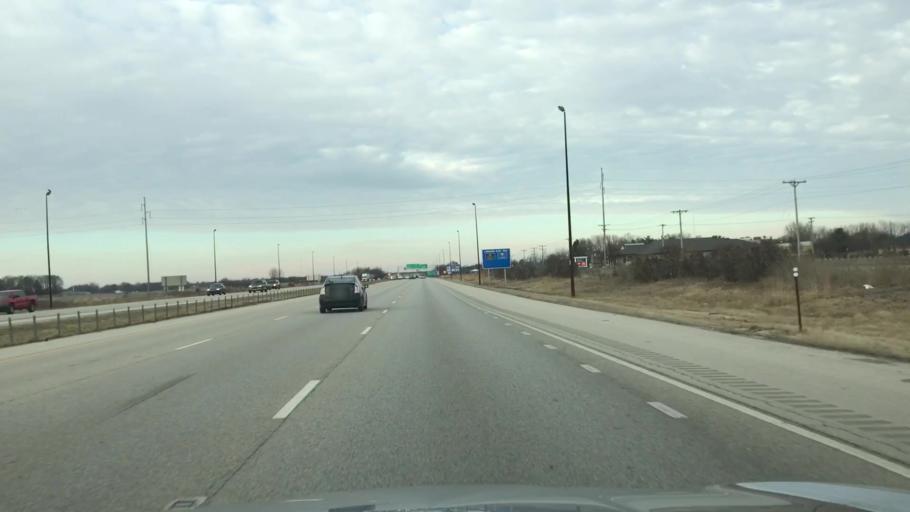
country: US
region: Illinois
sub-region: Sangamon County
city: Southern View
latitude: 39.7171
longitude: -89.6516
